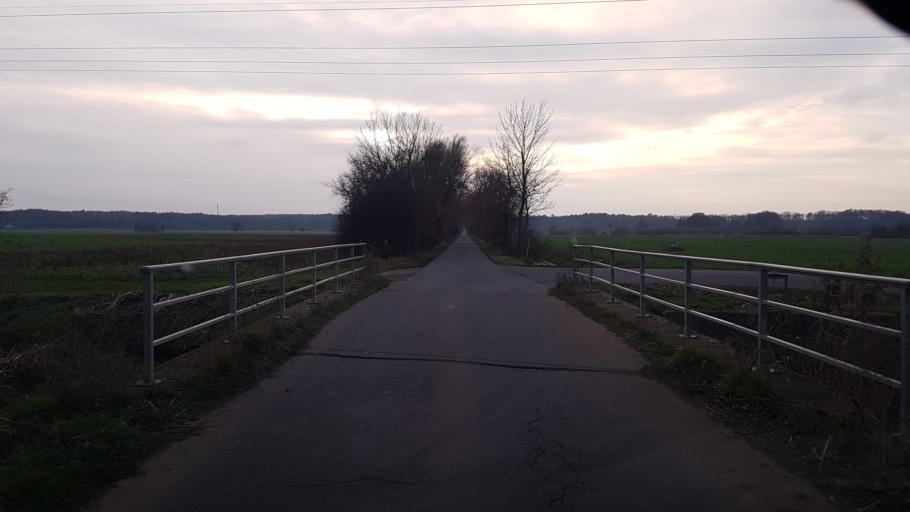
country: DE
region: Brandenburg
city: Ziltendorf
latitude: 52.2200
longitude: 14.6257
